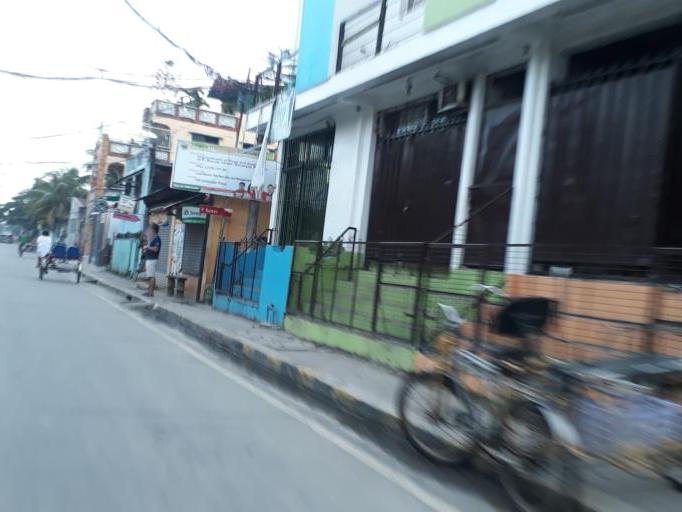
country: PH
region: Central Luzon
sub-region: Province of Bulacan
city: Obando
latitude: 14.7024
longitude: 120.9494
